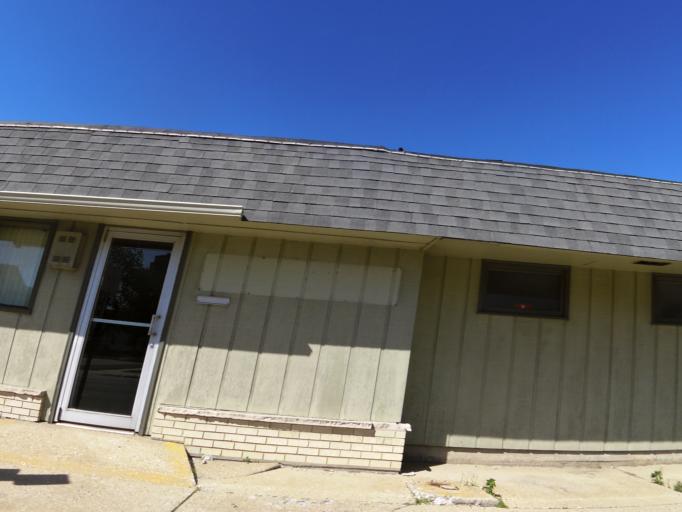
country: US
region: Illinois
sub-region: Winnebago County
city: Rockford
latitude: 42.2683
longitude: -89.0832
